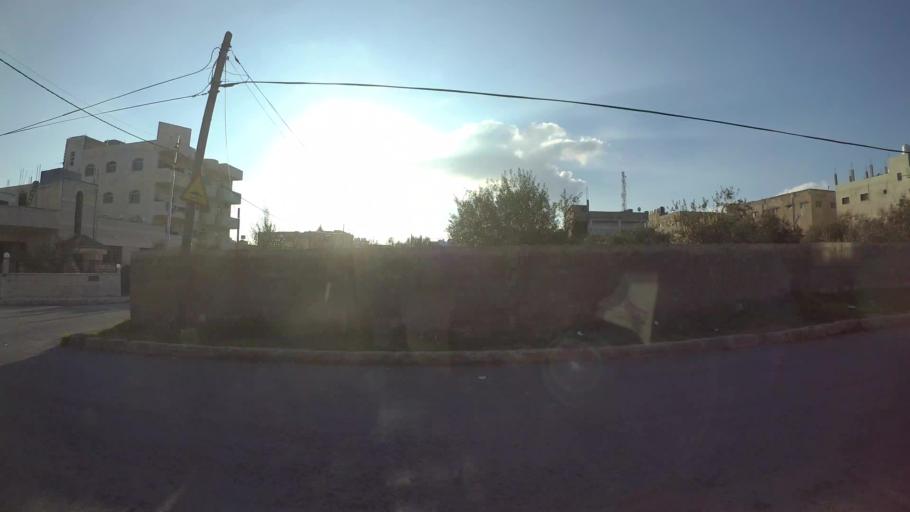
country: JO
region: Amman
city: Al Bunayyat ash Shamaliyah
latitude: 31.9021
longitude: 35.9090
